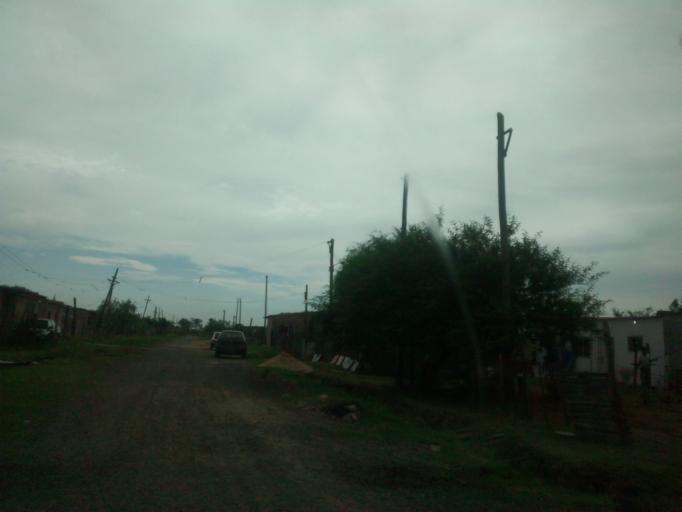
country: AR
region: Chaco
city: Fontana
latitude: -27.4663
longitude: -59.0335
